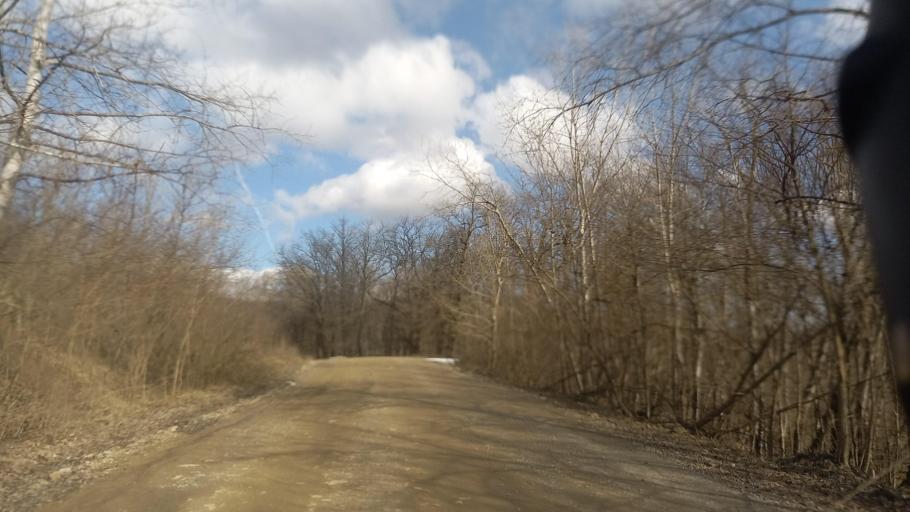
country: RU
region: Krasnodarskiy
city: Smolenskaya
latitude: 44.5998
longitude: 38.8425
